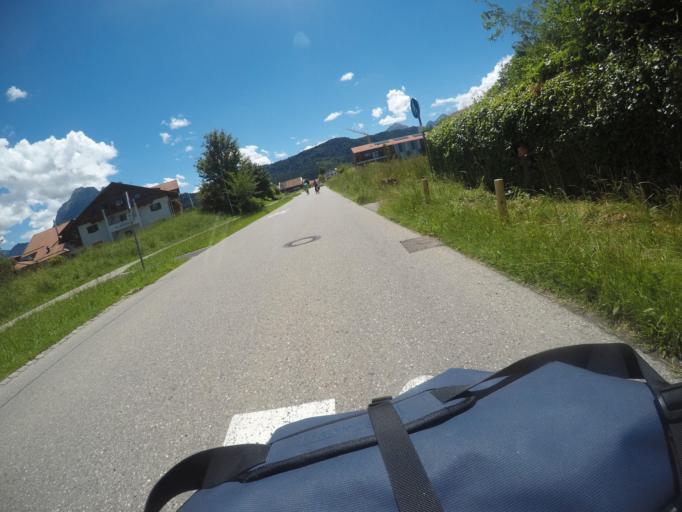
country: DE
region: Bavaria
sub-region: Swabia
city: Fuessen
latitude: 47.5803
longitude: 10.7091
